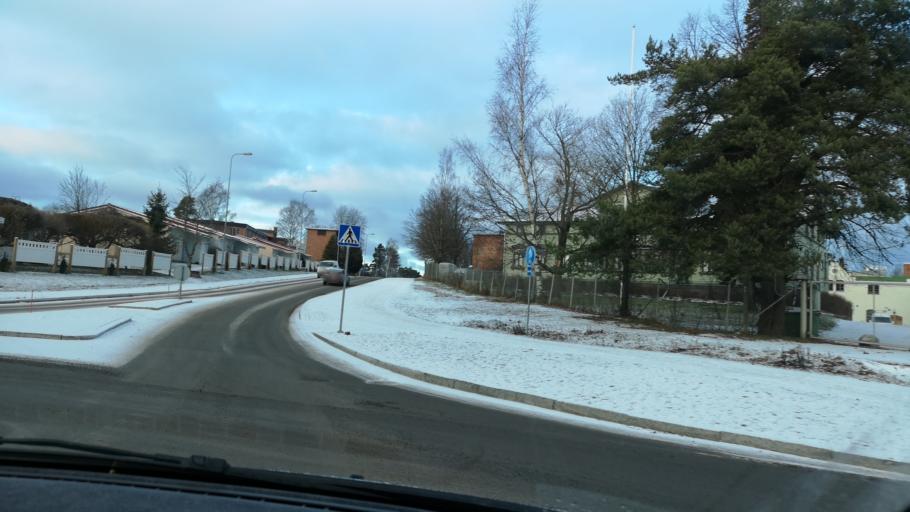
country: FI
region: Ostrobothnia
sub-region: Vaasa
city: Vaasa
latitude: 63.1161
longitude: 21.6183
